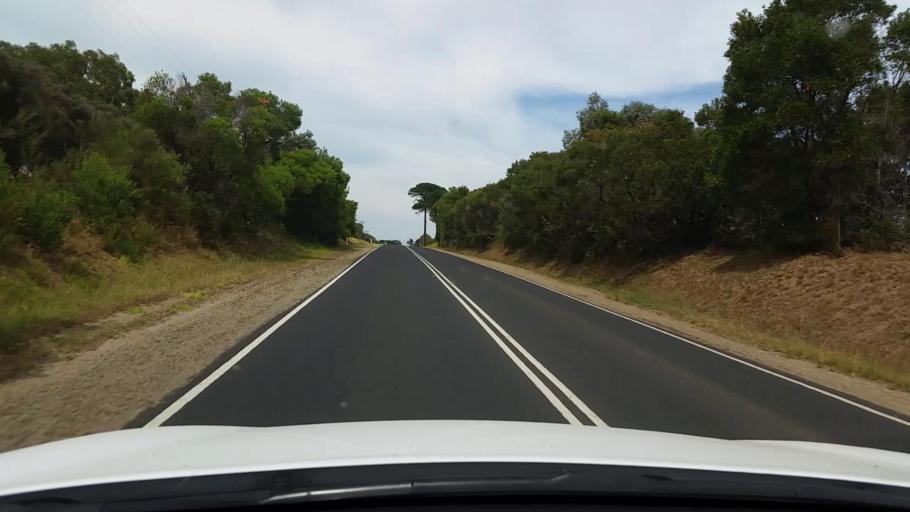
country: AU
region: Victoria
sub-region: Mornington Peninsula
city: Merricks
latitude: -38.4408
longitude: 145.0359
